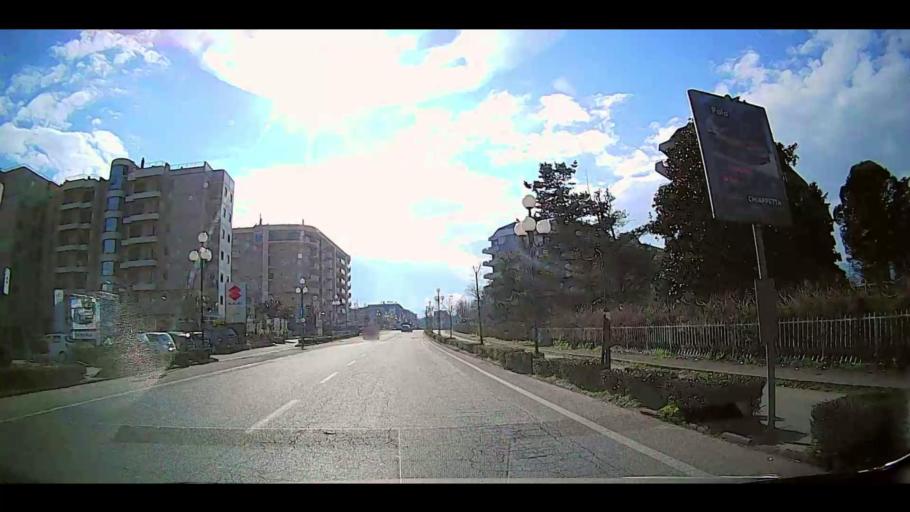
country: IT
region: Calabria
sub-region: Provincia di Cosenza
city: Quattromiglia
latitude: 39.3422
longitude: 16.2425
